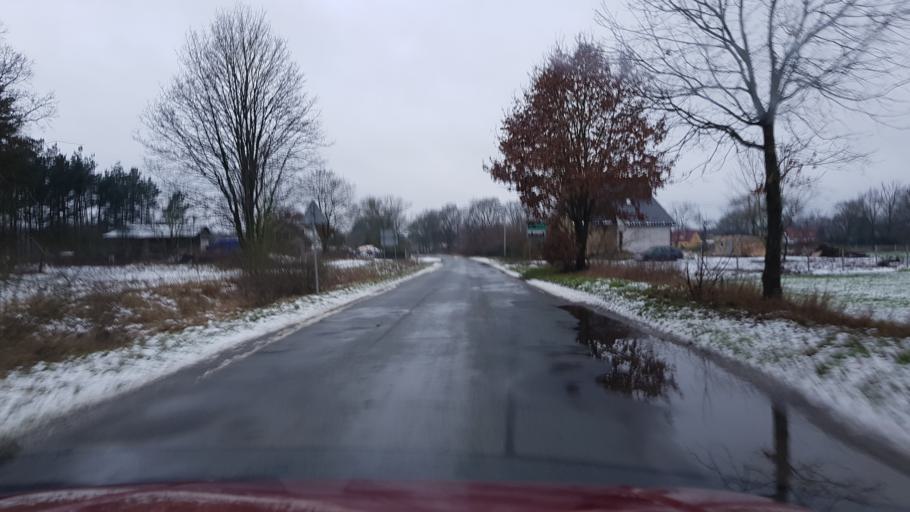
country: PL
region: West Pomeranian Voivodeship
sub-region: Powiat goleniowski
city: Nowogard
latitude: 53.6763
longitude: 15.2214
